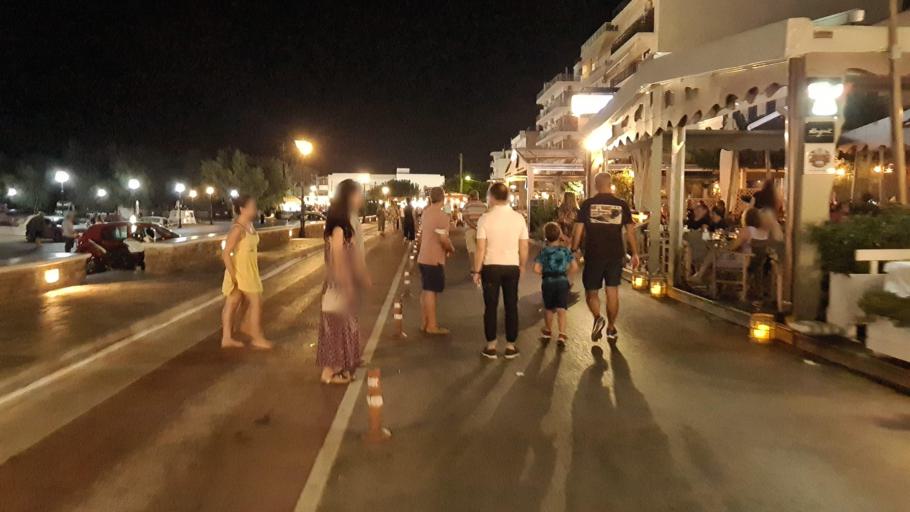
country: GR
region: Central Greece
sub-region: Nomos Evvoias
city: Karystos
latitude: 38.0134
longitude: 24.4176
